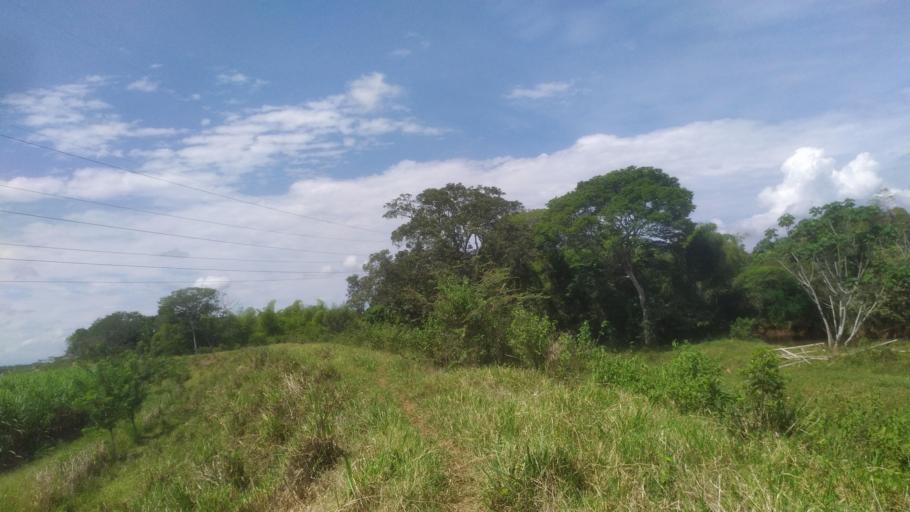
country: CO
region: Valle del Cauca
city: Jamundi
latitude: 3.2852
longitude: -76.5325
